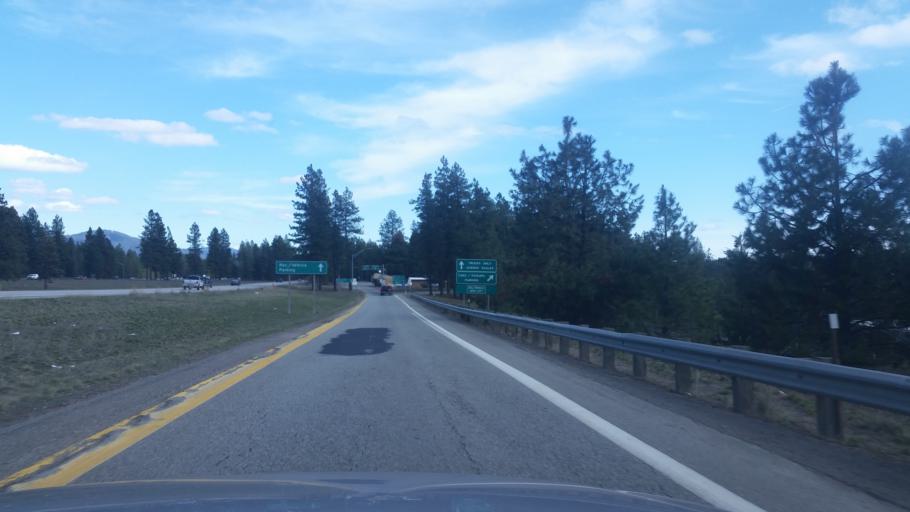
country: US
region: Idaho
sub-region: Kootenai County
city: Post Falls
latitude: 47.7084
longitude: -116.8708
